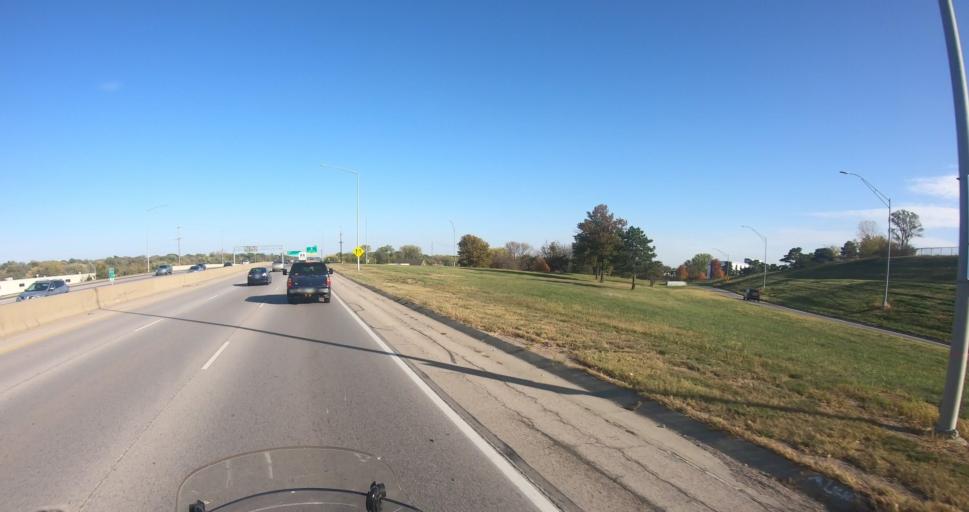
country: US
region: Iowa
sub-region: Polk County
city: Windsor Heights
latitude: 41.5938
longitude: -93.7182
